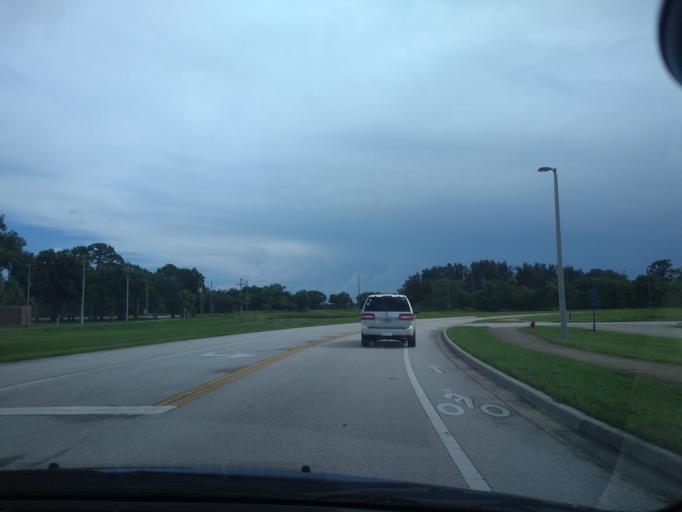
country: US
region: Florida
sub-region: Indian River County
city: West Vero Corridor
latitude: 27.6333
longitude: -80.4552
